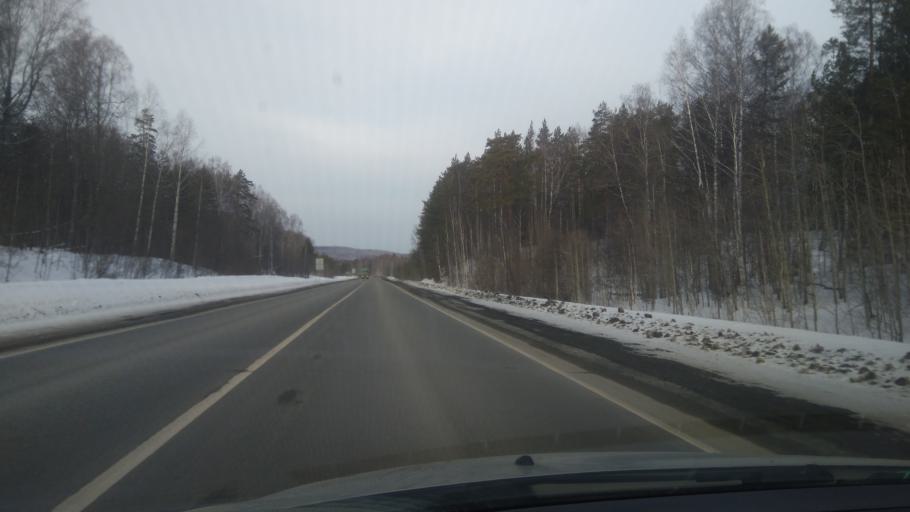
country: RU
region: Sverdlovsk
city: Bisert'
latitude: 56.8359
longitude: 58.8831
